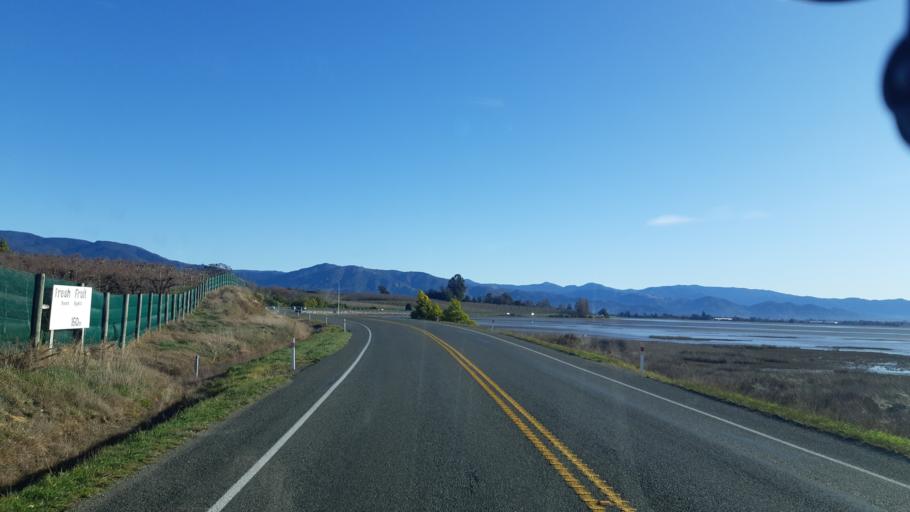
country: NZ
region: Tasman
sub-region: Tasman District
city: Motueka
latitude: -41.1608
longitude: 173.0226
